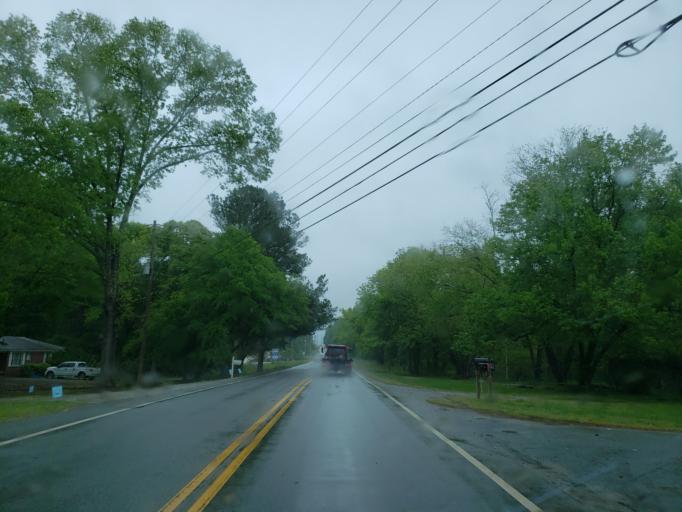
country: US
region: Georgia
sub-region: Paulding County
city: Hiram
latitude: 33.8832
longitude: -84.7587
